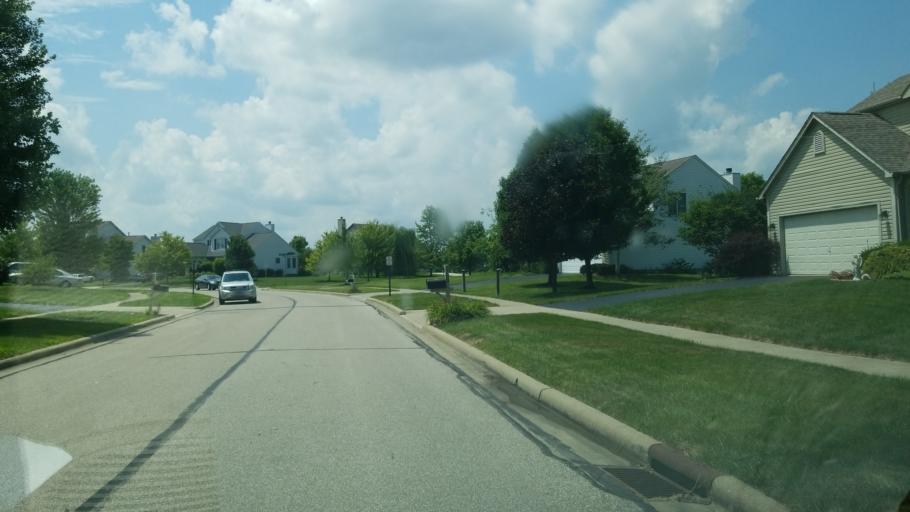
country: US
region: Ohio
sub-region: Delaware County
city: Lewis Center
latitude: 40.2184
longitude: -82.9972
